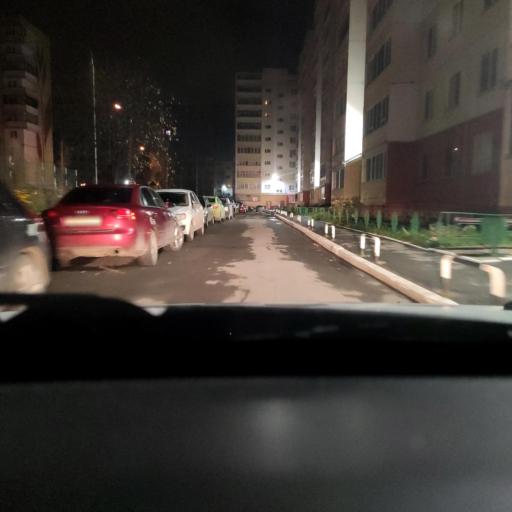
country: RU
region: Perm
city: Kondratovo
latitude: 58.0469
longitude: 56.0826
